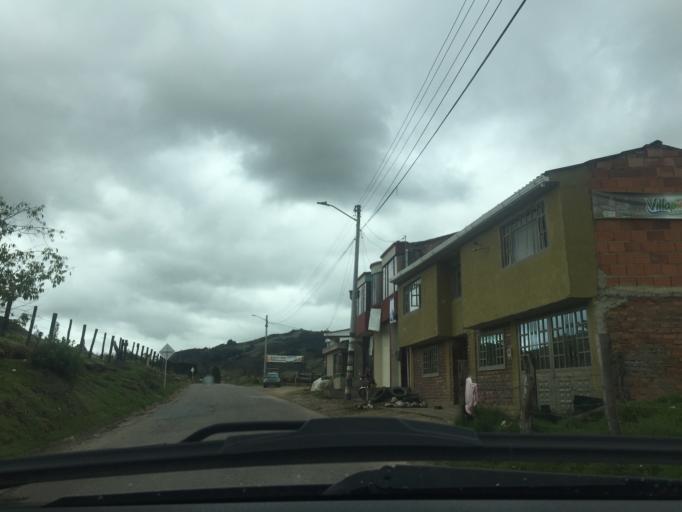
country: CO
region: Cundinamarca
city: Villapinzon
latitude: 5.2221
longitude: -73.6075
